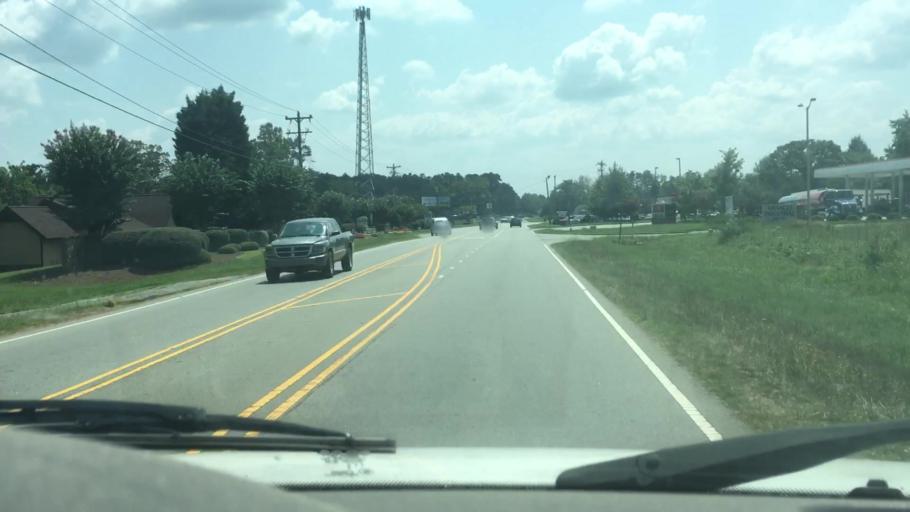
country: US
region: North Carolina
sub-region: Lincoln County
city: Westport
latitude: 35.4851
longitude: -80.9948
